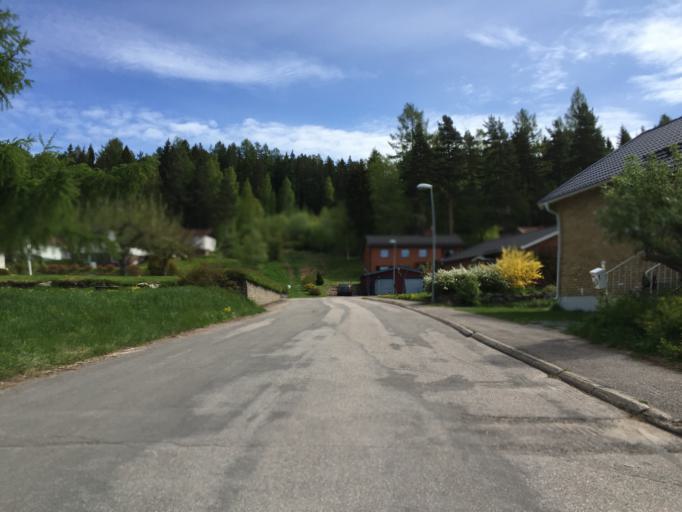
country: SE
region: Dalarna
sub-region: Ludvika Kommun
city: Ludvika
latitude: 60.1350
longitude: 15.1821
